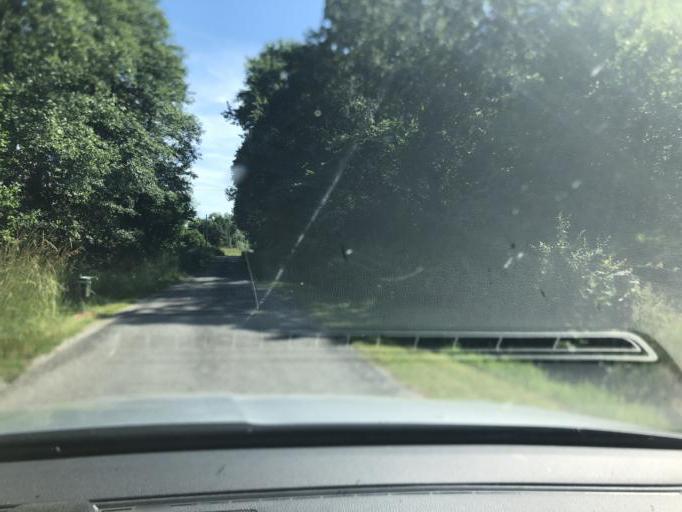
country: SE
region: Blekinge
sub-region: Karlshamns Kommun
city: Morrum
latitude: 56.1794
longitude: 14.7034
